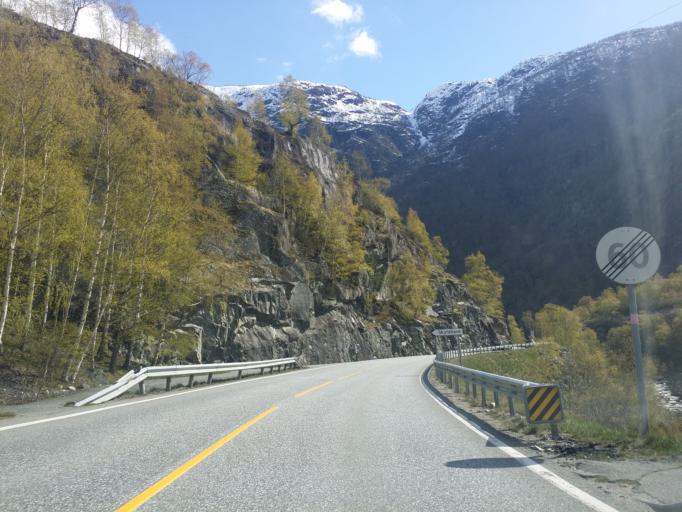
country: NO
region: Hordaland
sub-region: Eidfjord
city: Eidfjord
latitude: 60.4216
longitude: 7.1413
